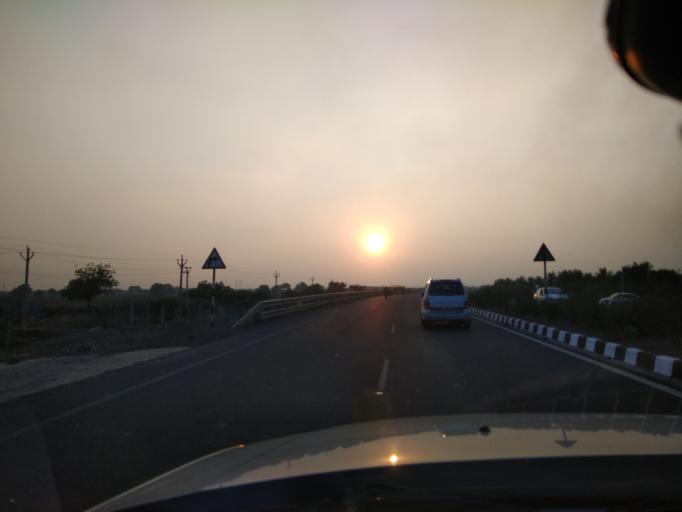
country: IN
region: Gujarat
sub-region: Jamnagar
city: Bedi
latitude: 22.4438
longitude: 69.9996
